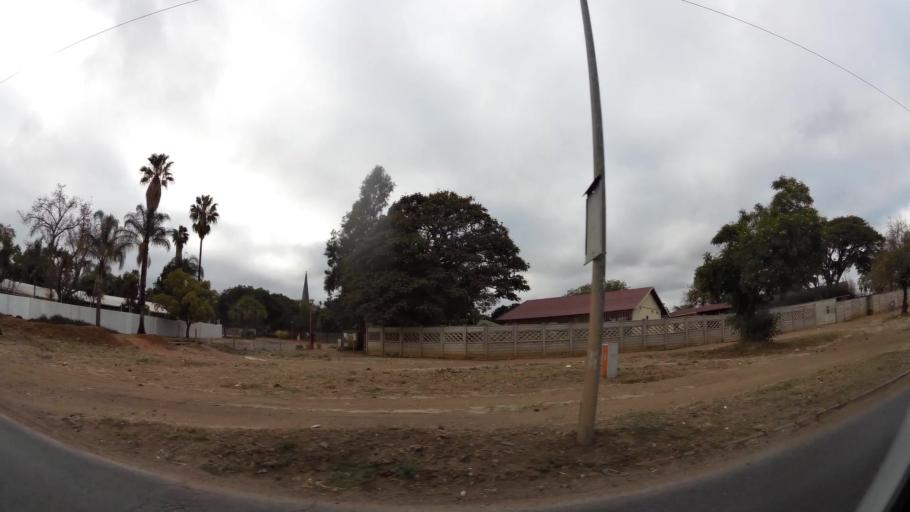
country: ZA
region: Limpopo
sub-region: Capricorn District Municipality
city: Polokwane
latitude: -23.8916
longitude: 29.4530
